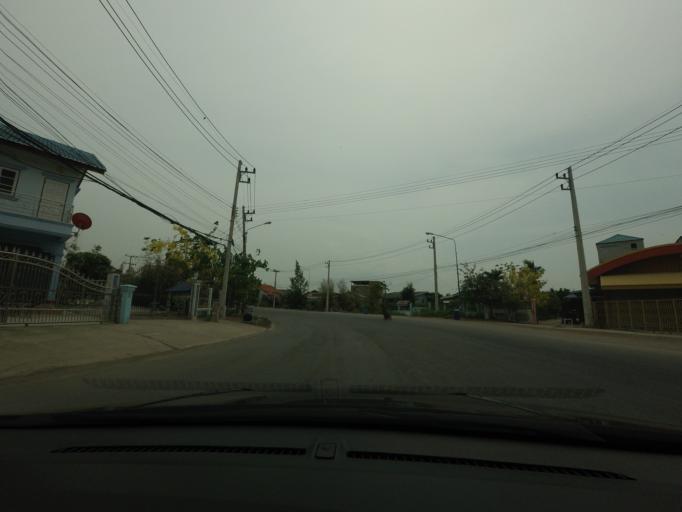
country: TH
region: Phetchaburi
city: Ban Laem
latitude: 13.2100
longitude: 99.9746
